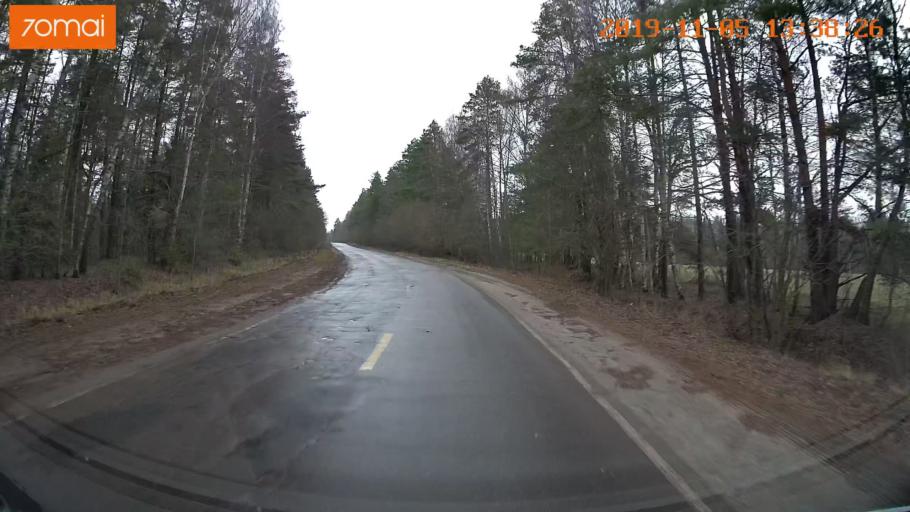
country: RU
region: Ivanovo
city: Shuya
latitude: 56.9318
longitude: 41.3866
